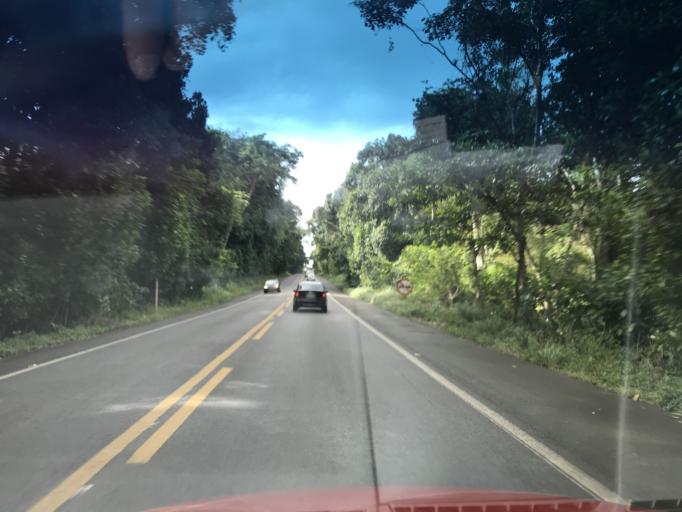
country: BR
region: Bahia
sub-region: Itajuipe
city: Itajuipe
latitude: -14.6326
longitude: -39.3346
